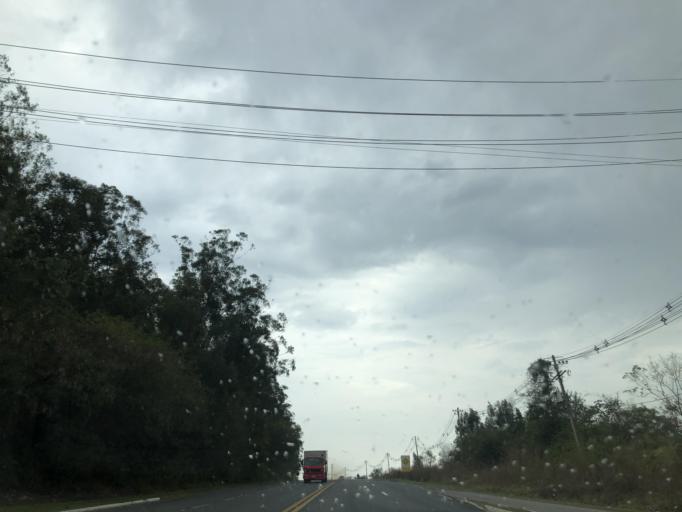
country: BR
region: Sao Paulo
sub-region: Salto De Pirapora
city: Salto de Pirapora
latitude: -23.6601
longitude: -47.5917
